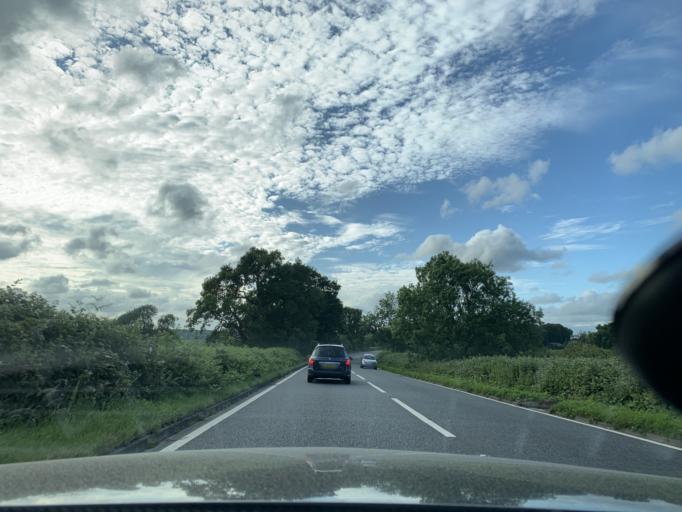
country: GB
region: England
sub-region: East Sussex
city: Robertsbridge
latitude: 50.9694
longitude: 0.4779
